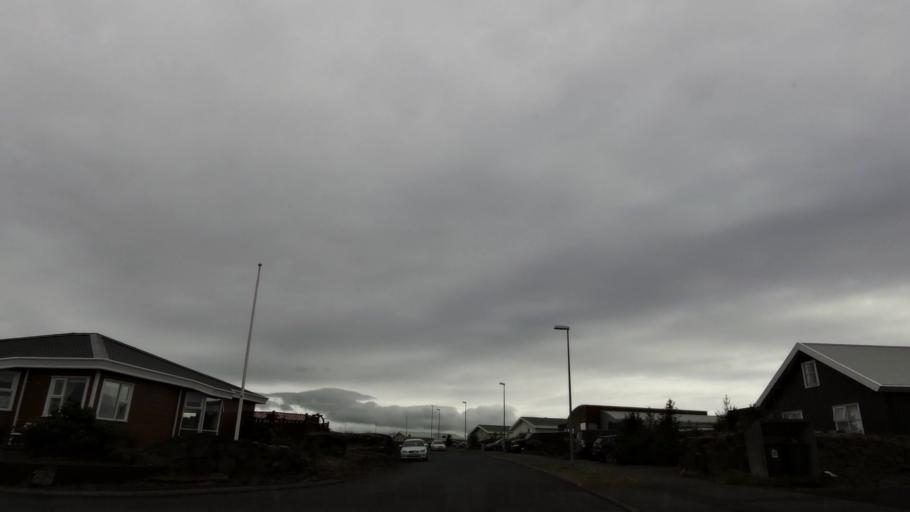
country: IS
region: Capital Region
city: Alftanes
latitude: 64.0558
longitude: -21.9930
